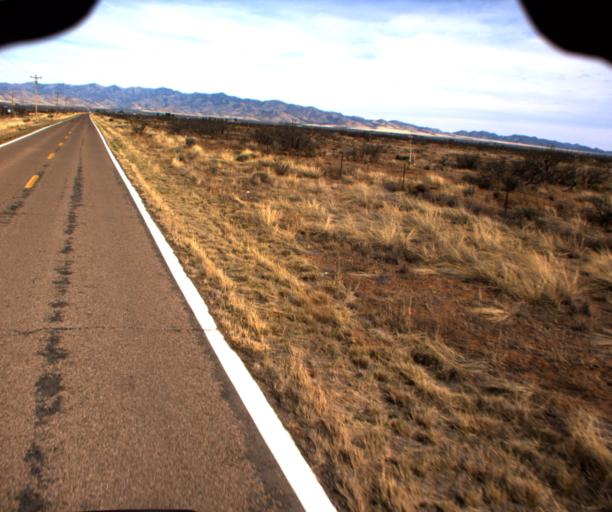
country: US
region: Arizona
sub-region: Cochise County
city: Willcox
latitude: 31.8762
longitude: -109.5992
